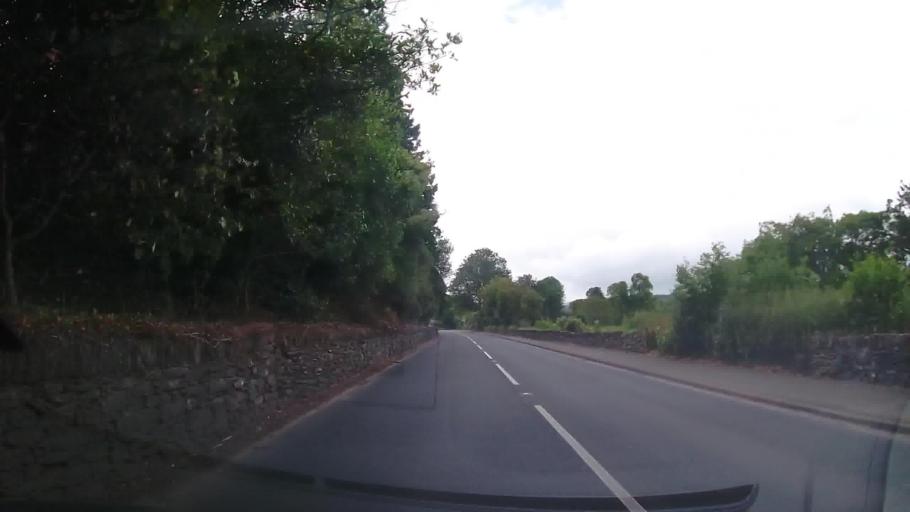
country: GB
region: Wales
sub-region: Denbighshire
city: Corwen
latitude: 52.9791
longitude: -3.3601
